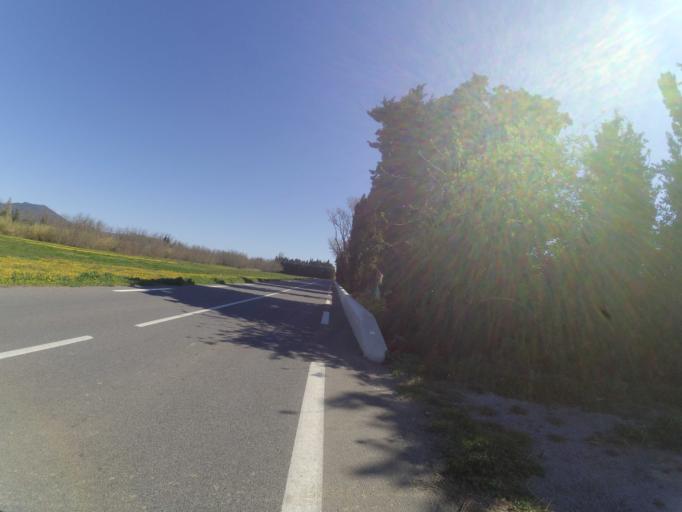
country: FR
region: Languedoc-Roussillon
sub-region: Departement des Pyrenees-Orientales
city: Millas
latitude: 42.6840
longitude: 2.6968
